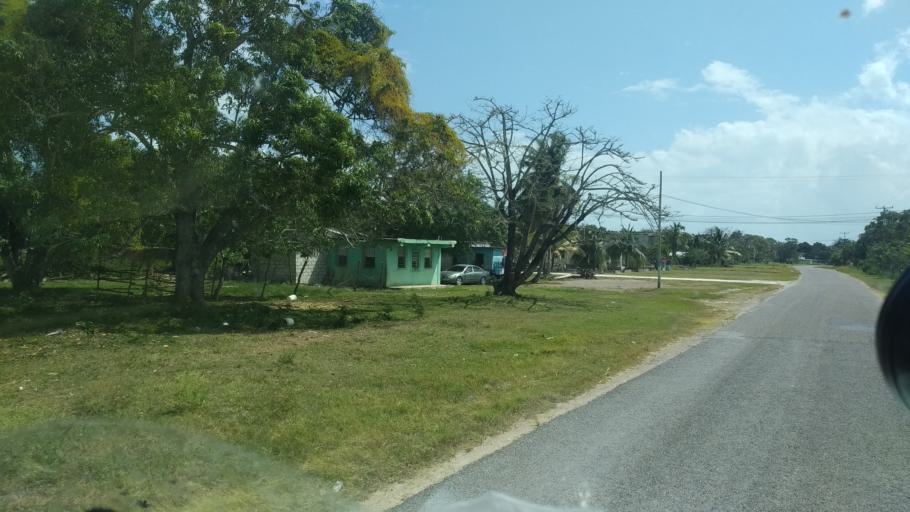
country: BZ
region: Corozal
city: Corozal
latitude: 18.3901
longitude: -88.4189
